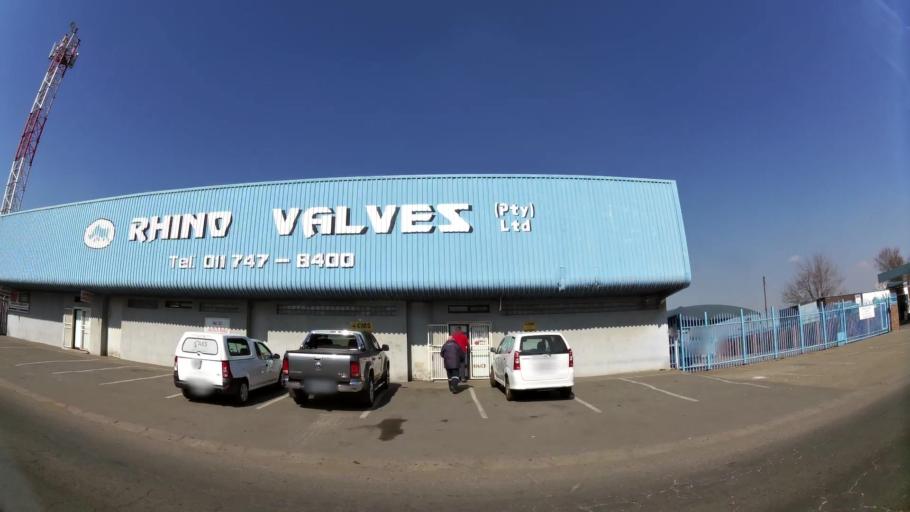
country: ZA
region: Gauteng
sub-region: Ekurhuleni Metropolitan Municipality
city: Benoni
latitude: -26.2079
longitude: 28.2948
